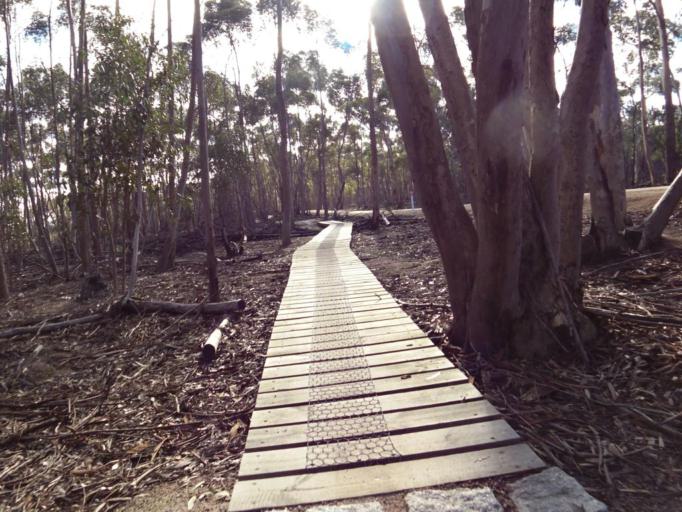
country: AU
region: Victoria
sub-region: Greater Geelong
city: Lara
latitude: -37.9420
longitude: 144.4113
